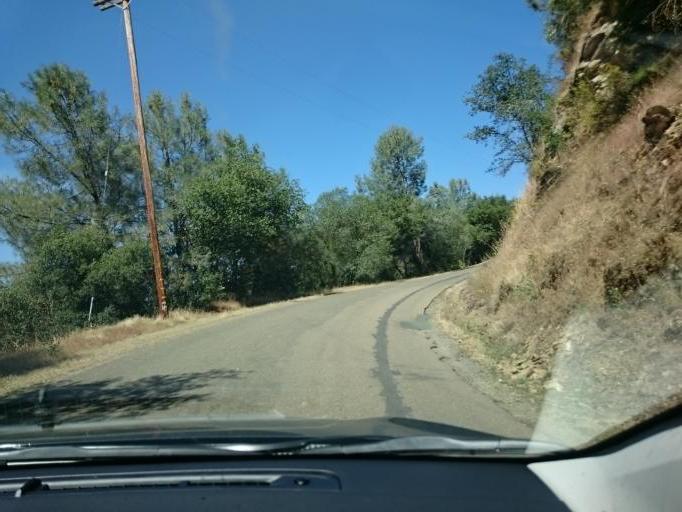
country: US
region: California
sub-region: Calaveras County
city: Rancho Calaveras
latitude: 38.1156
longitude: -120.8018
